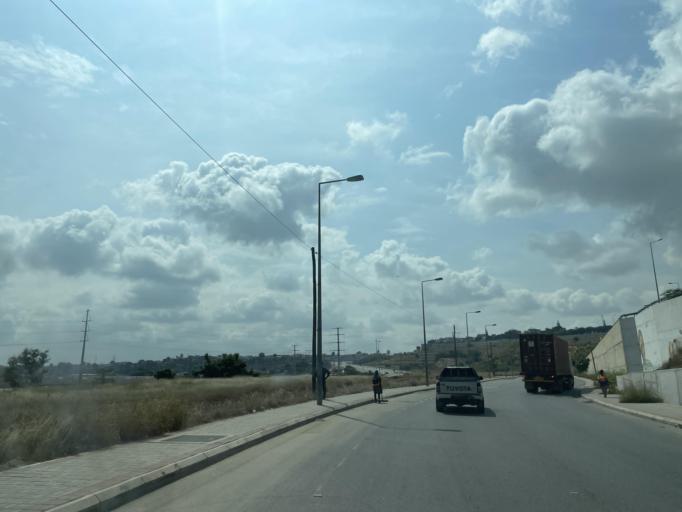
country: AO
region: Luanda
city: Luanda
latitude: -8.8045
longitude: 13.2510
